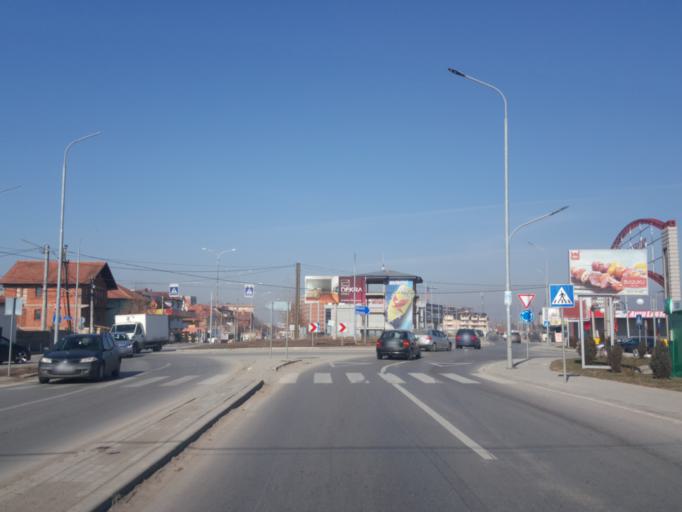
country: XK
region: Mitrovica
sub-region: Vushtrri
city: Vushtrri
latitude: 42.8147
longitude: 20.9834
